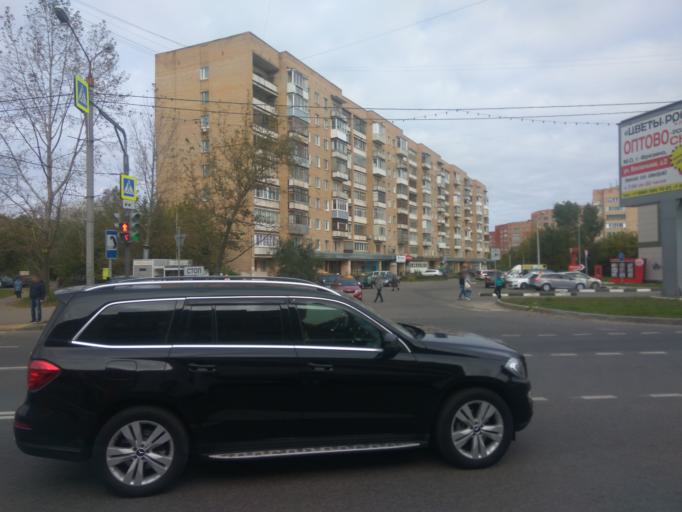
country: RU
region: Moskovskaya
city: Fryazino
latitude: 55.9550
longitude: 38.0588
